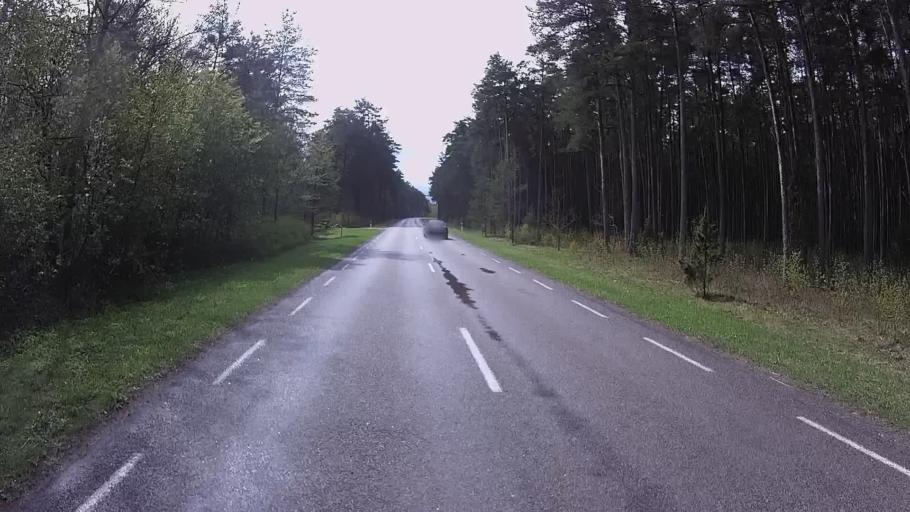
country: EE
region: Hiiumaa
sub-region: Kaerdla linn
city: Kardla
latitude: 58.7187
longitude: 22.6161
